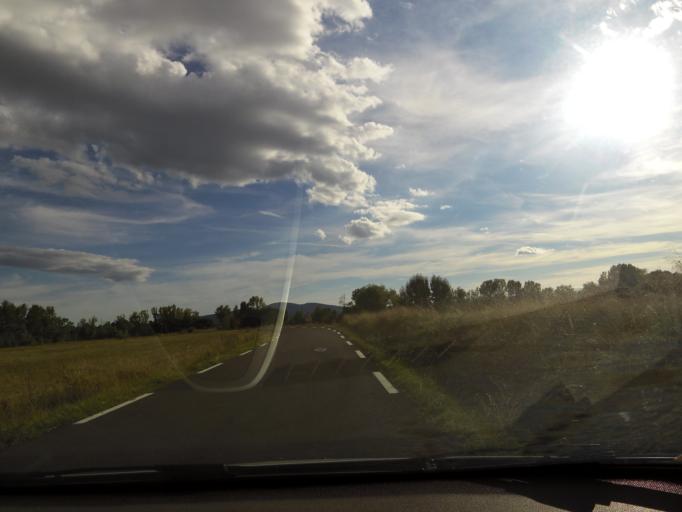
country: FR
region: Languedoc-Roussillon
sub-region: Departement du Gard
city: Lezan
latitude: 43.9696
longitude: 4.0452
